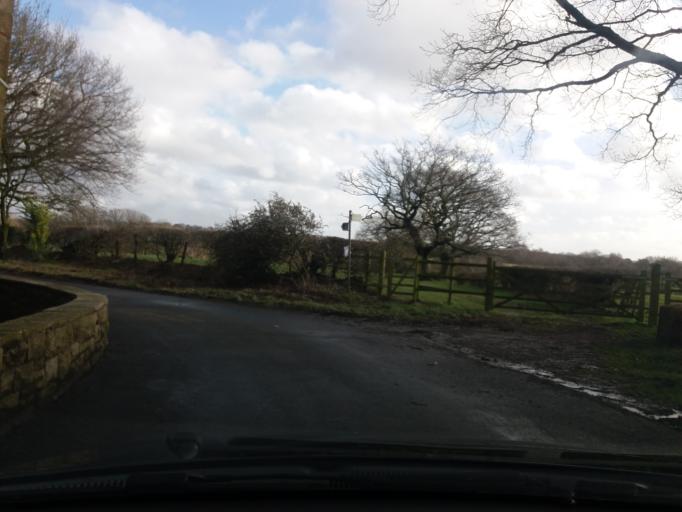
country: GB
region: England
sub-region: Lancashire
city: Adlington
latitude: 53.6058
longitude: -2.6135
